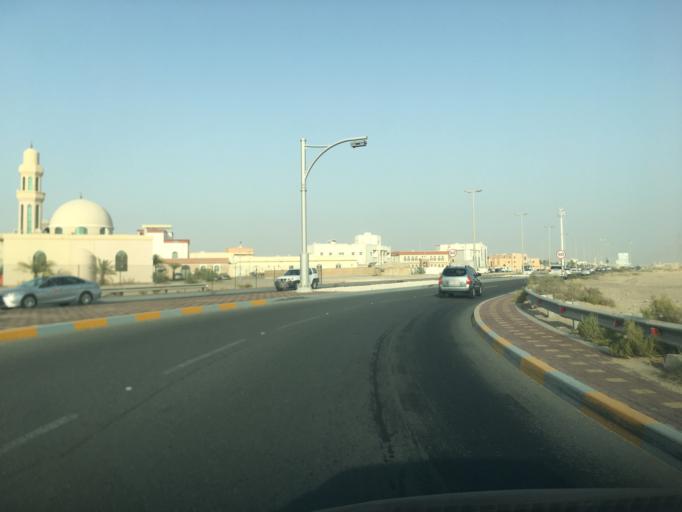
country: AE
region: Abu Dhabi
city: Abu Dhabi
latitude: 24.3225
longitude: 54.6275
